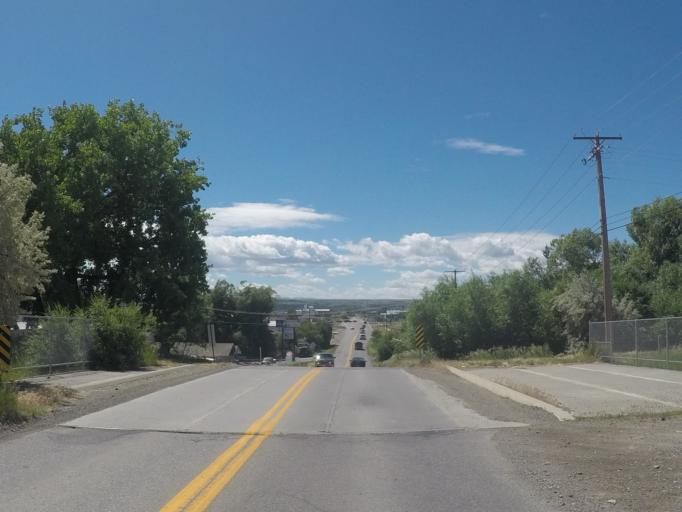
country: US
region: Montana
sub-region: Yellowstone County
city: Billings
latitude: 45.7486
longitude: -108.5968
